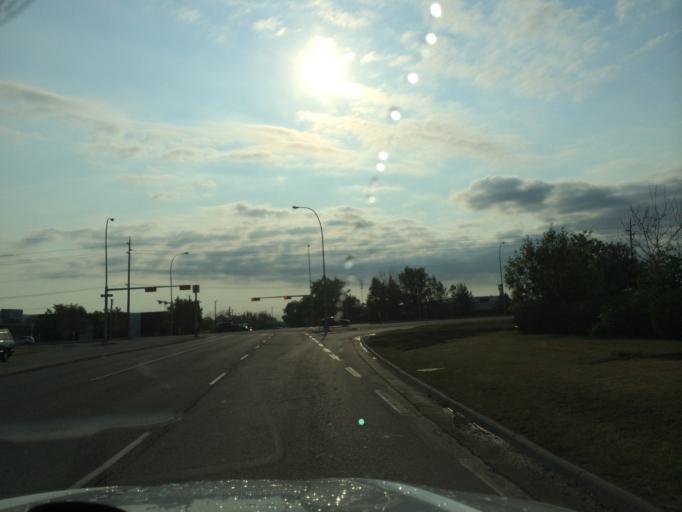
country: CA
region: Alberta
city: Calgary
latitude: 51.0865
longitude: -114.0031
